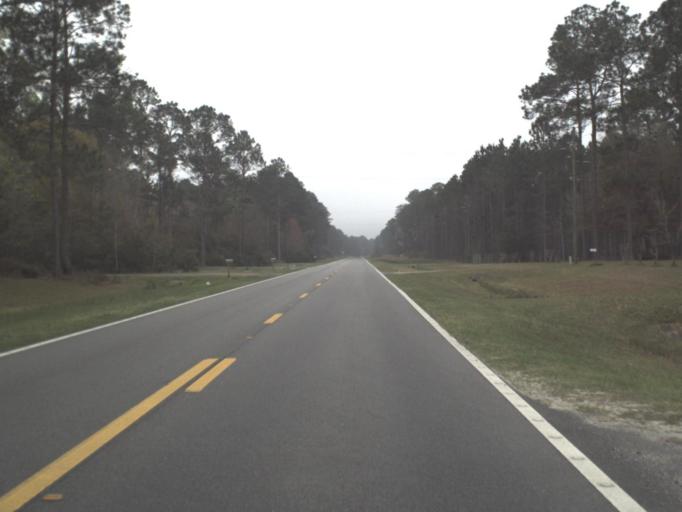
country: US
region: Florida
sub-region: Liberty County
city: Bristol
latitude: 30.3315
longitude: -84.8234
